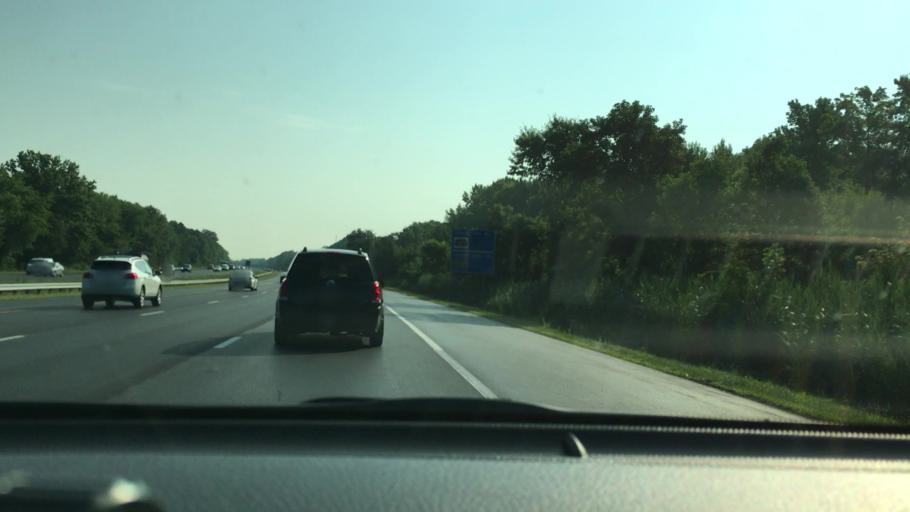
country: US
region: New Jersey
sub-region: Burlington County
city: Ramblewood
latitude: 39.9481
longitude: -74.9327
